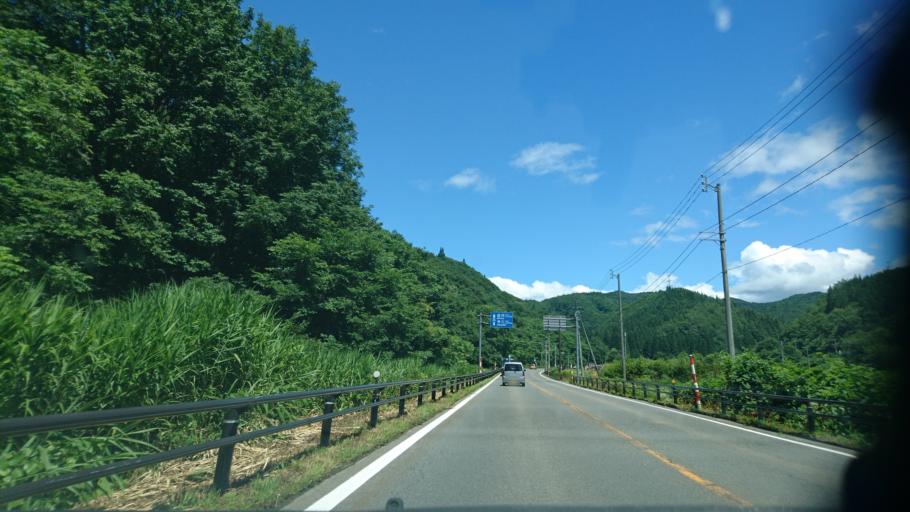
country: JP
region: Akita
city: Kakunodatemachi
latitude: 39.6562
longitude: 140.6722
